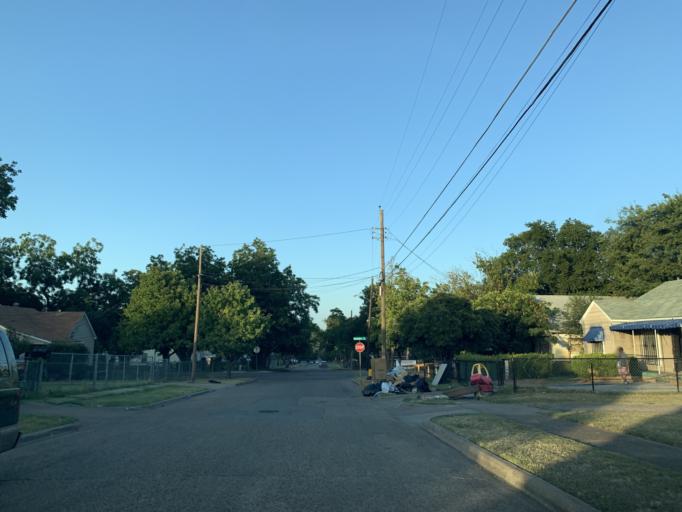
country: US
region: Texas
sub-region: Dallas County
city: Dallas
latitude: 32.6982
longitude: -96.8049
